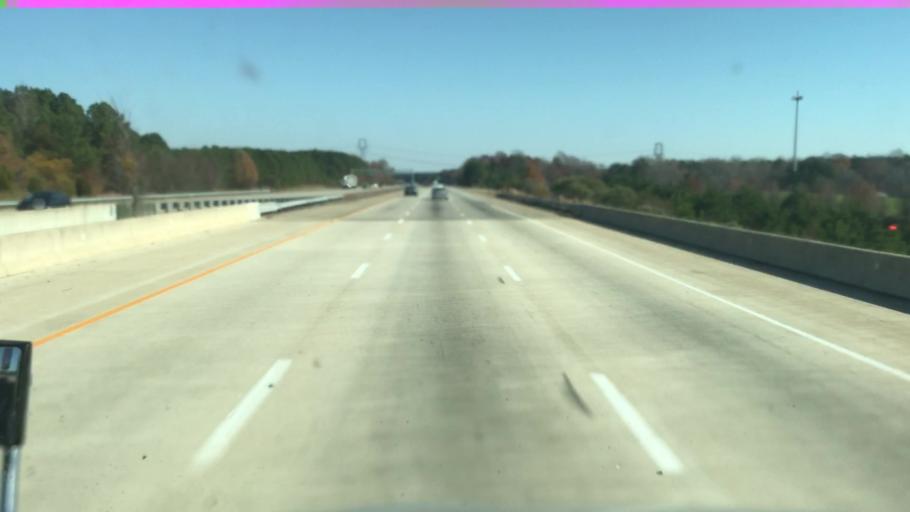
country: US
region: North Carolina
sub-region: Wake County
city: Knightdale
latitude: 35.7674
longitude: -78.4653
